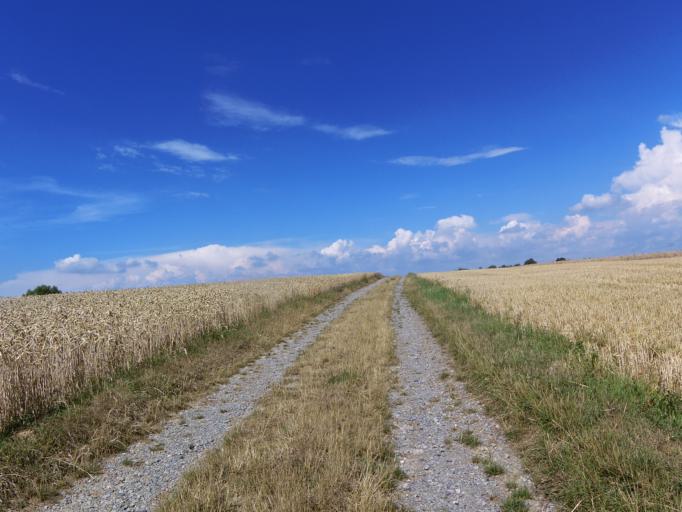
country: DE
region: Bavaria
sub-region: Regierungsbezirk Unterfranken
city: Estenfeld
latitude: 49.8336
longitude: 9.9840
